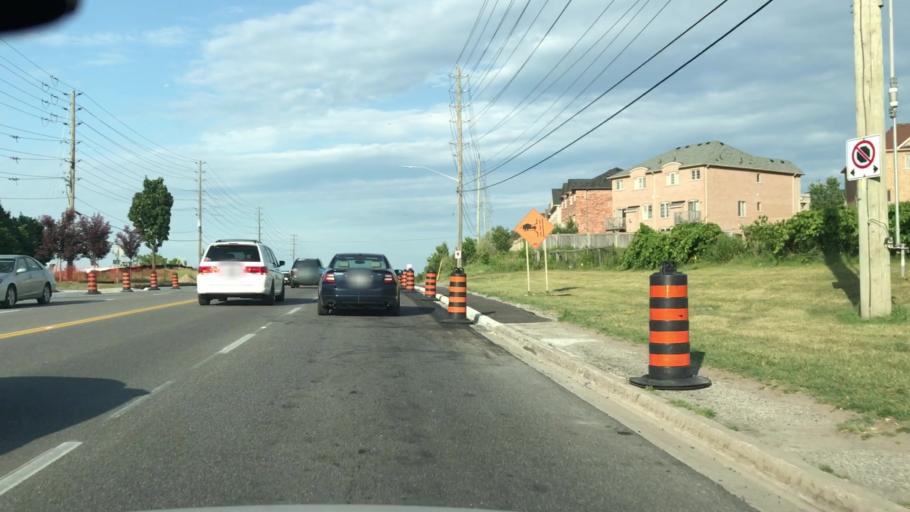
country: CA
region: Ontario
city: Newmarket
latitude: 44.0462
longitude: -79.4329
